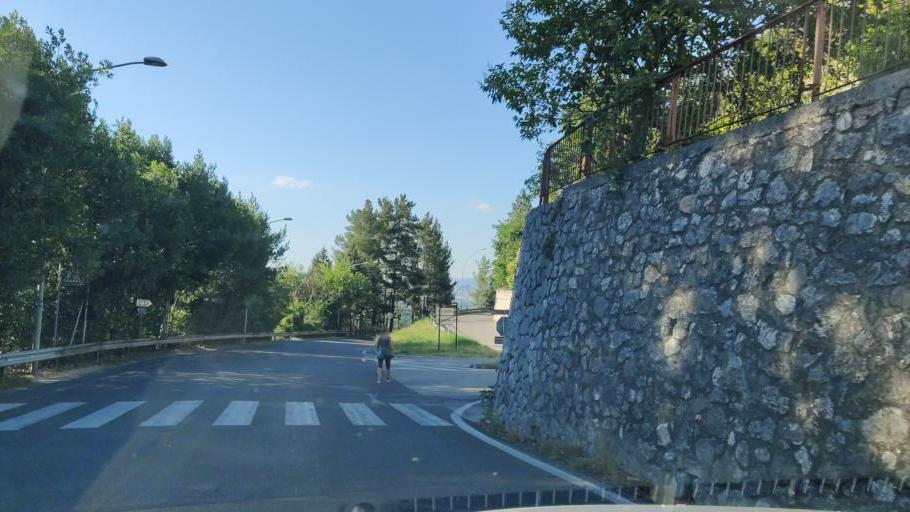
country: IT
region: Umbria
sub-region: Provincia di Terni
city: Narni
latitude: 42.5161
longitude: 12.5252
